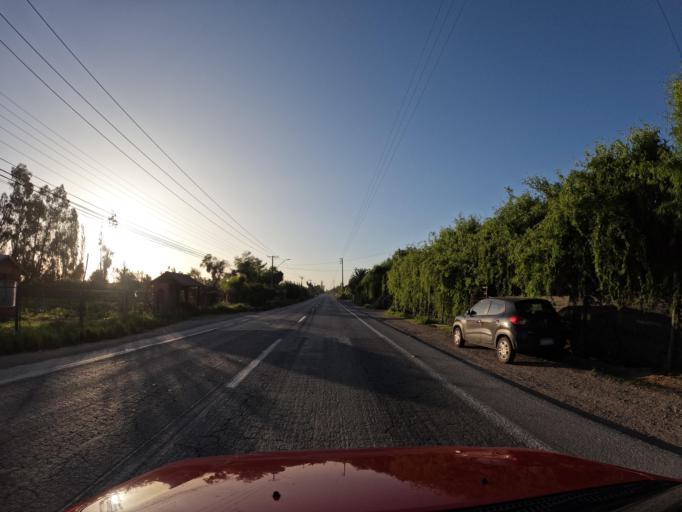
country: CL
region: O'Higgins
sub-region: Provincia de Cachapoal
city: San Vicente
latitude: -34.2663
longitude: -71.3711
